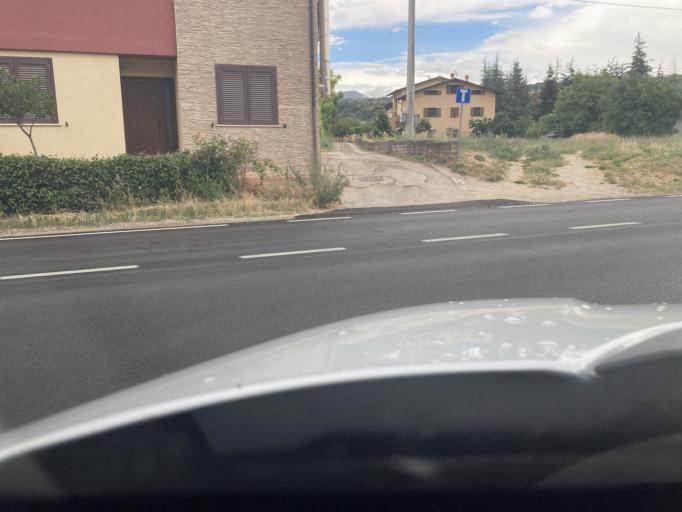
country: IT
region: Abruzzo
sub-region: Provincia dell' Aquila
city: Sant'Eusanio Forconese
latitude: 42.2957
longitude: 13.5351
